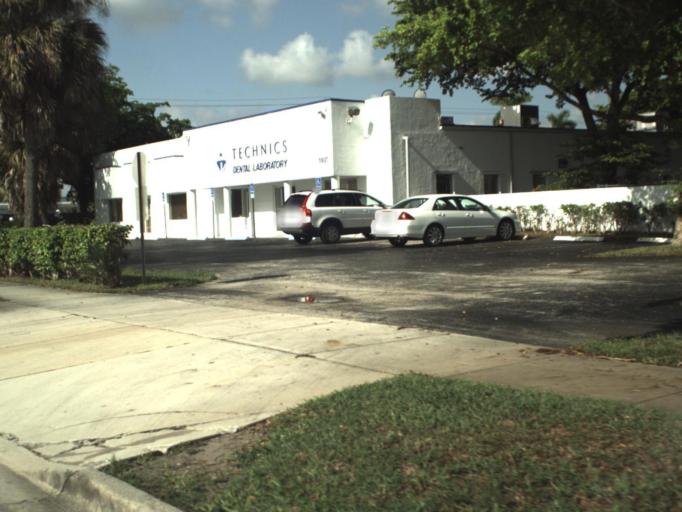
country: US
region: Florida
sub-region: Broward County
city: Margate
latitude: 26.2506
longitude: -80.2016
